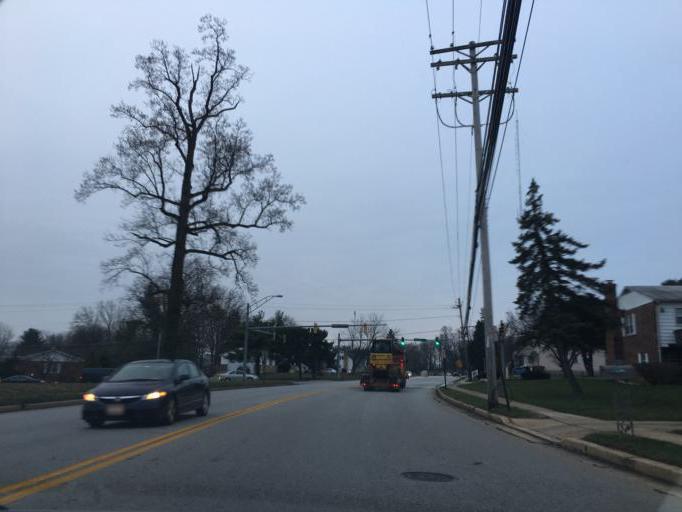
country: US
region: Maryland
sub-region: Baltimore County
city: Catonsville
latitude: 39.2912
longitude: -76.7523
